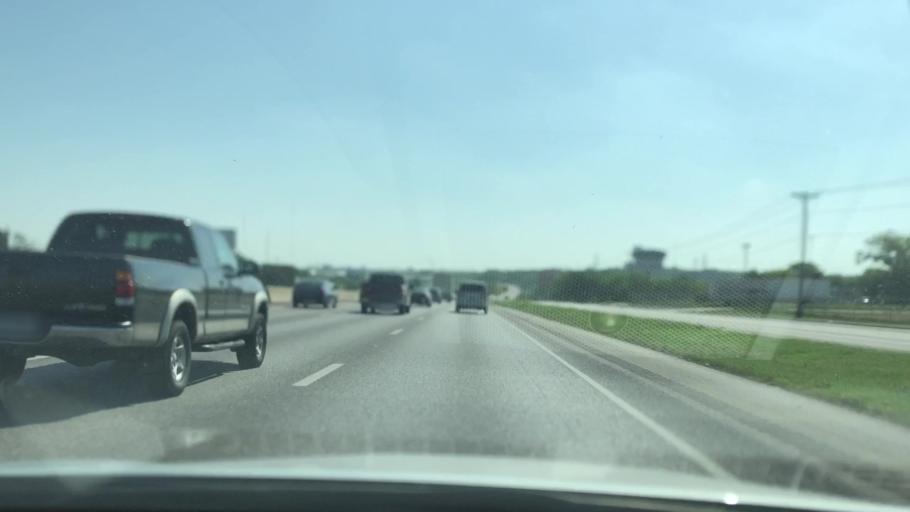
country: US
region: Texas
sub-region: Guadalupe County
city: Northcliff
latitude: 29.6599
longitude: -98.1754
